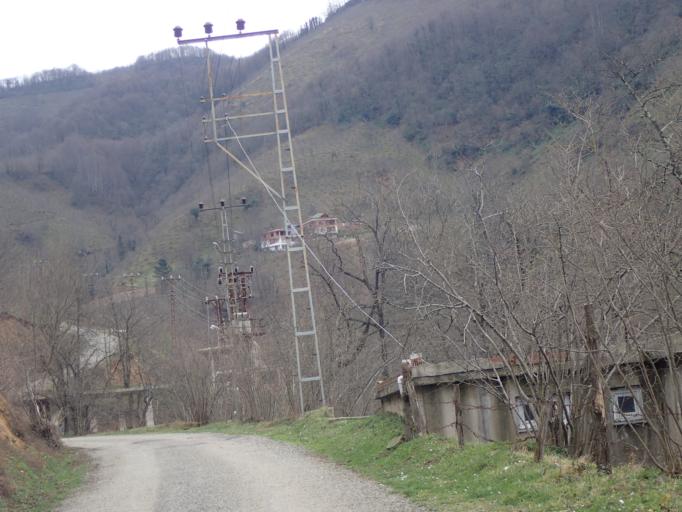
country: TR
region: Ordu
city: Camas
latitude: 40.8855
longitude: 37.5135
